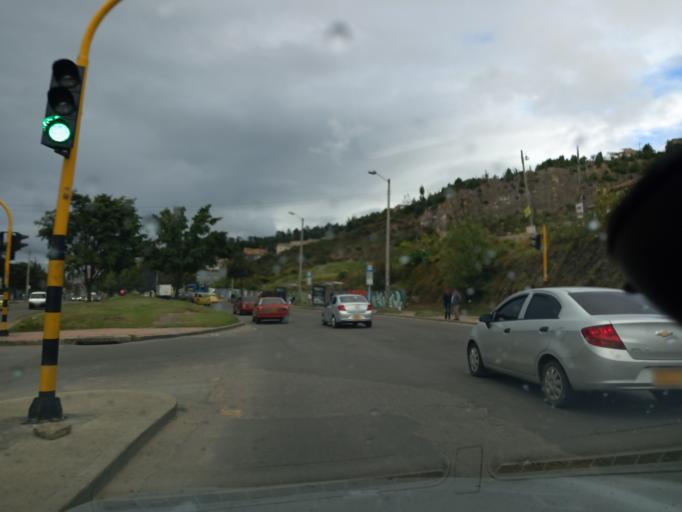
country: CO
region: Cundinamarca
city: La Calera
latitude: 4.7409
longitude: -74.0223
